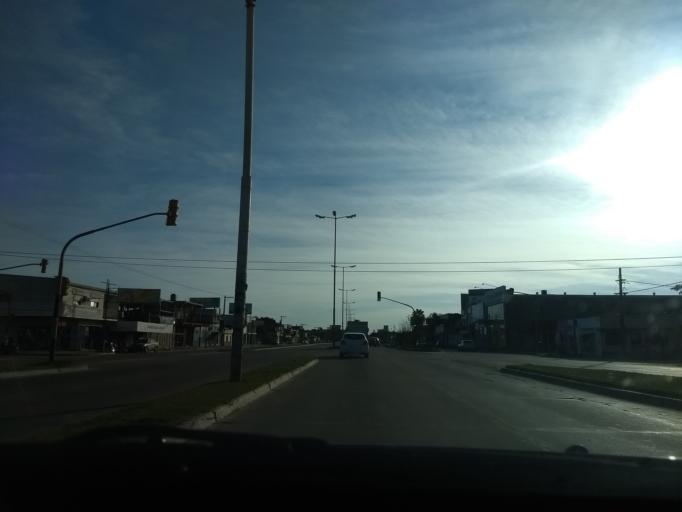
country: AR
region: Corrientes
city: Corrientes
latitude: -27.4794
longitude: -58.8072
